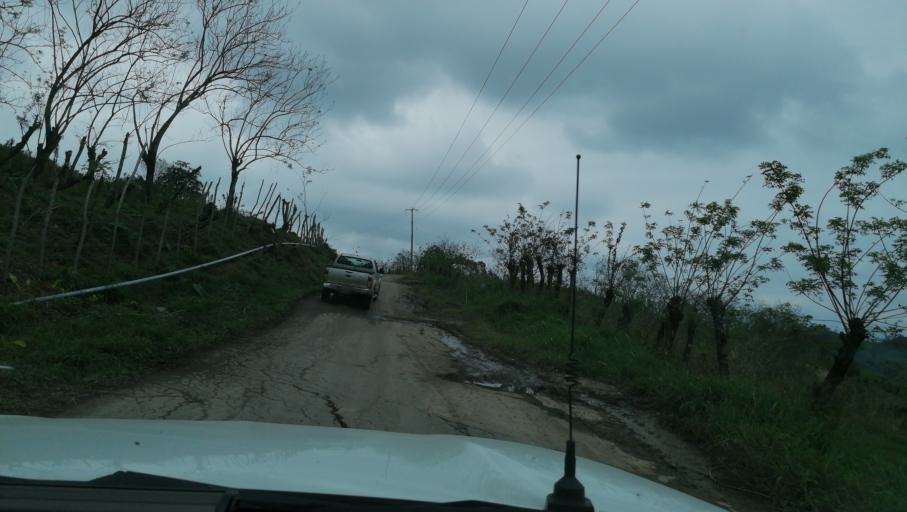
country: MX
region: Chiapas
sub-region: Francisco Leon
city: San Miguel la Sardina
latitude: 17.2740
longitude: -93.2678
